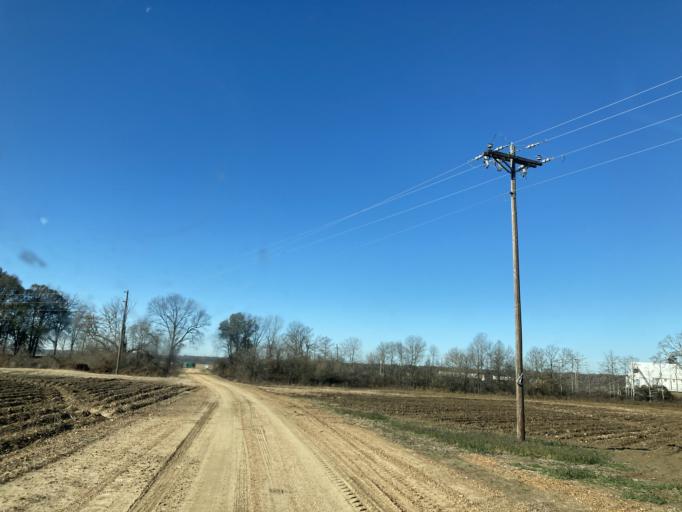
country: US
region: Mississippi
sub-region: Sharkey County
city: Rolling Fork
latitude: 32.8693
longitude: -90.6939
